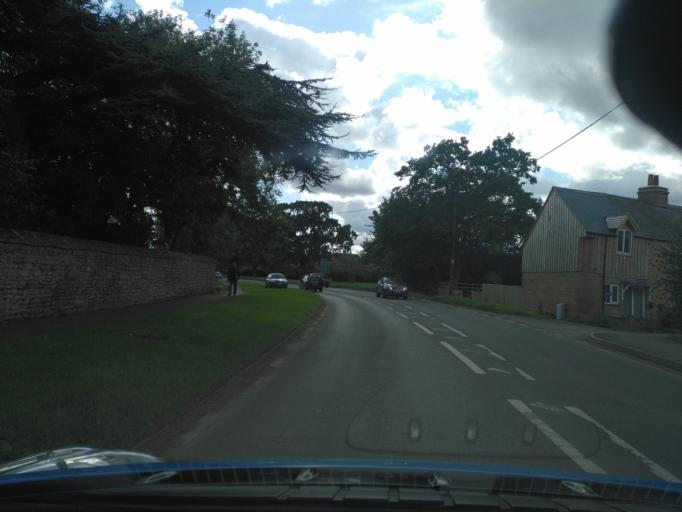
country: GB
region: England
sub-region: Oxfordshire
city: Sutton Courtenay
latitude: 51.6435
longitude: -1.3134
